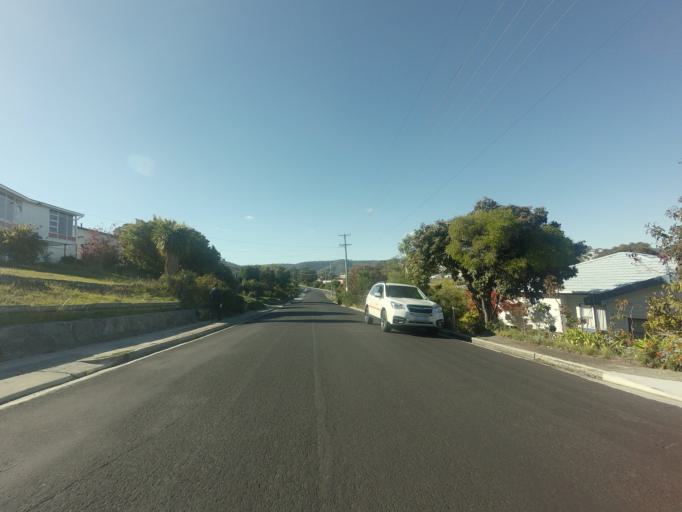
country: AU
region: Tasmania
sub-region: Clarence
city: Bellerive
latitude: -42.8714
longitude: 147.3617
